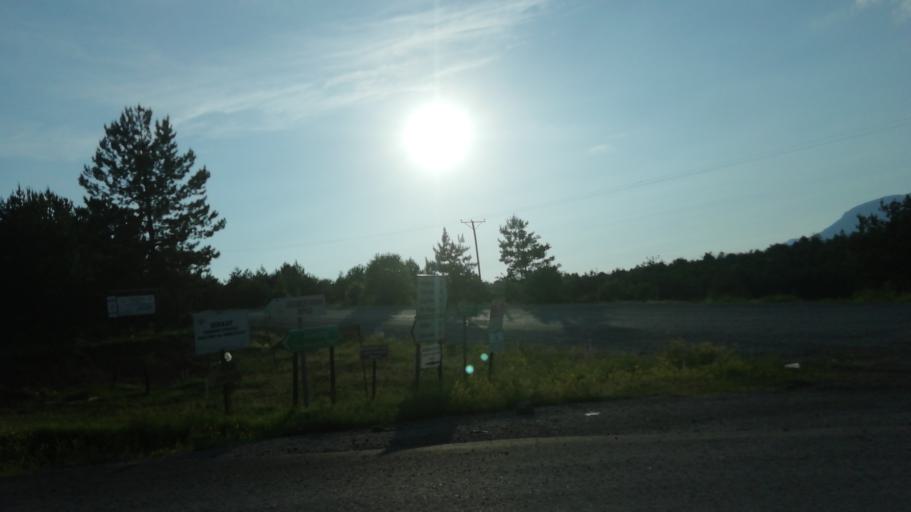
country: TR
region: Karabuk
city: Karabuk
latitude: 41.1276
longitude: 32.6047
